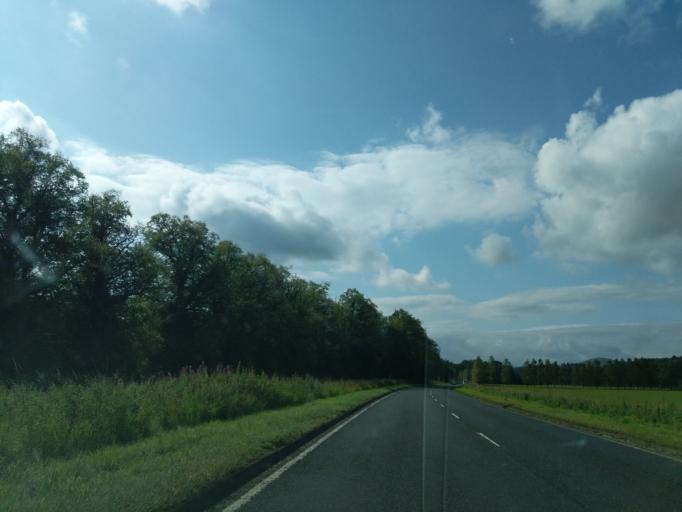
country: GB
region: Scotland
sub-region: The Scottish Borders
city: Peebles
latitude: 55.7181
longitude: -3.2046
